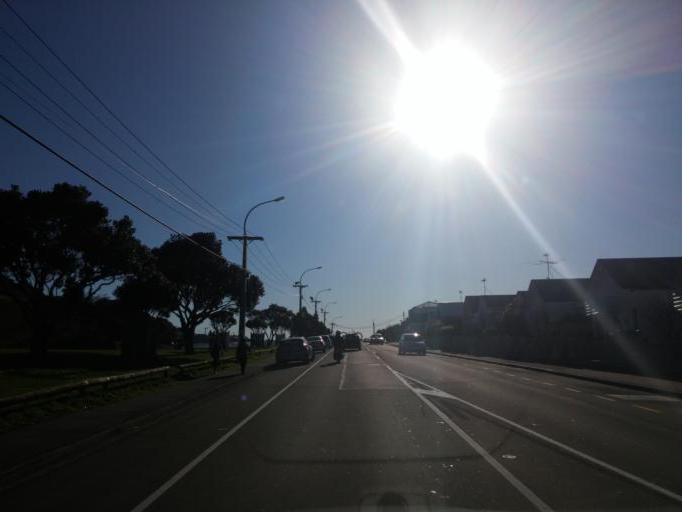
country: NZ
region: Wellington
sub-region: Wellington City
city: Brooklyn
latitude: -41.3173
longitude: 174.7754
